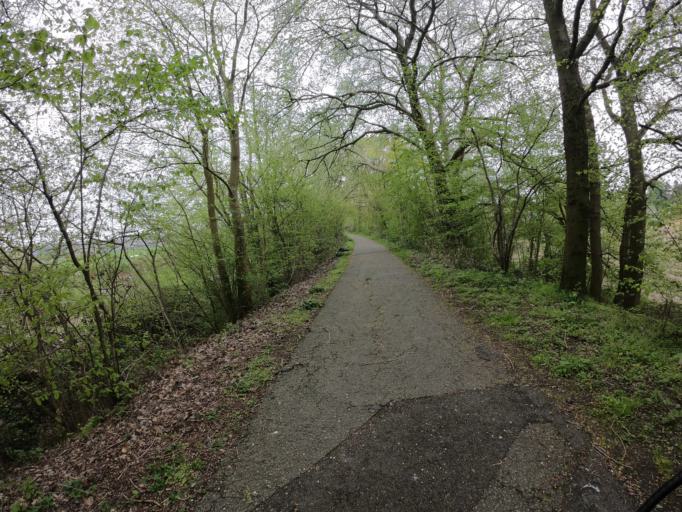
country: BE
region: Flanders
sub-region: Provincie Oost-Vlaanderen
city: Ronse
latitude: 50.7394
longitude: 3.6268
